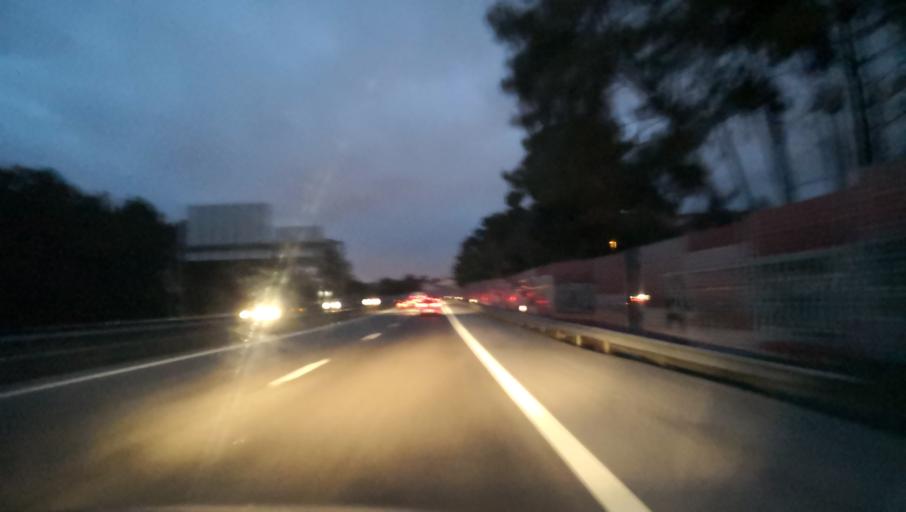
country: PT
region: Setubal
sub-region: Barreiro
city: Santo Antonio da Charneca
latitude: 38.6145
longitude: -9.0278
